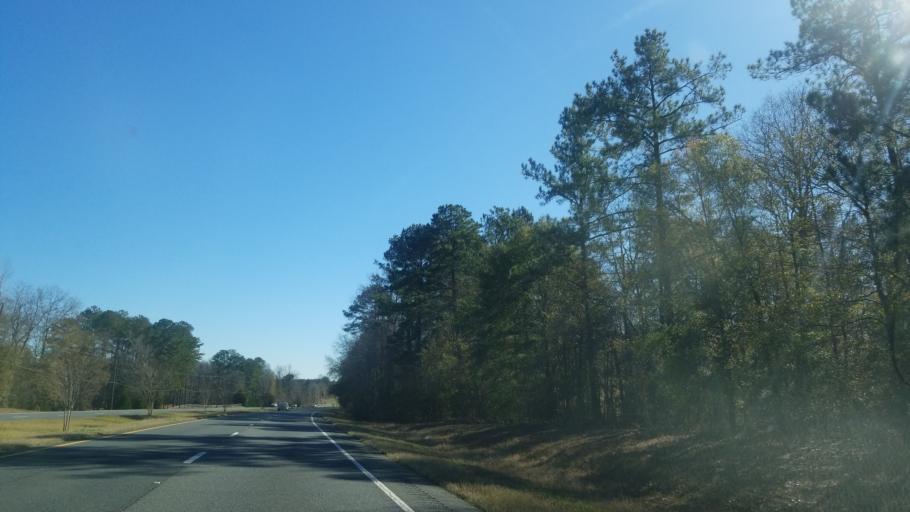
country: US
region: Georgia
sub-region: Talbot County
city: Talbotton
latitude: 32.5506
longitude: -84.7360
